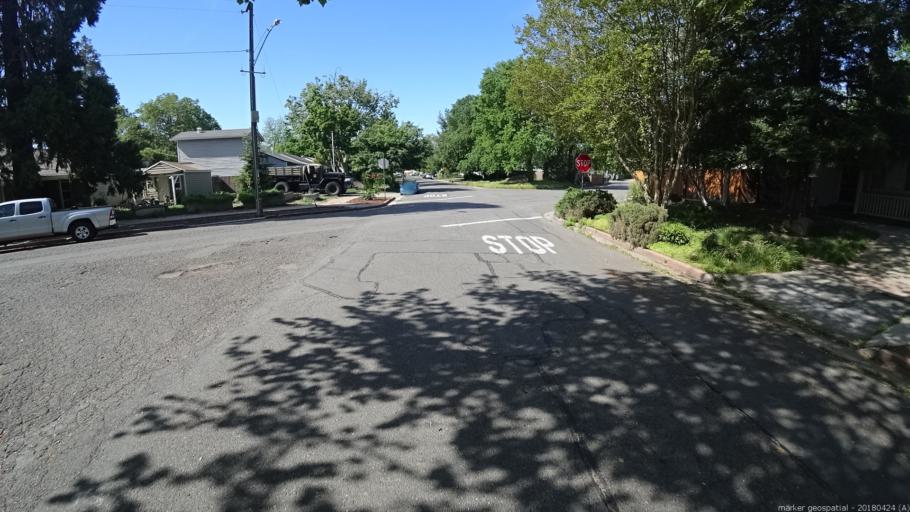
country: US
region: California
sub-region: Yolo County
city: West Sacramento
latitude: 38.5648
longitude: -121.5285
